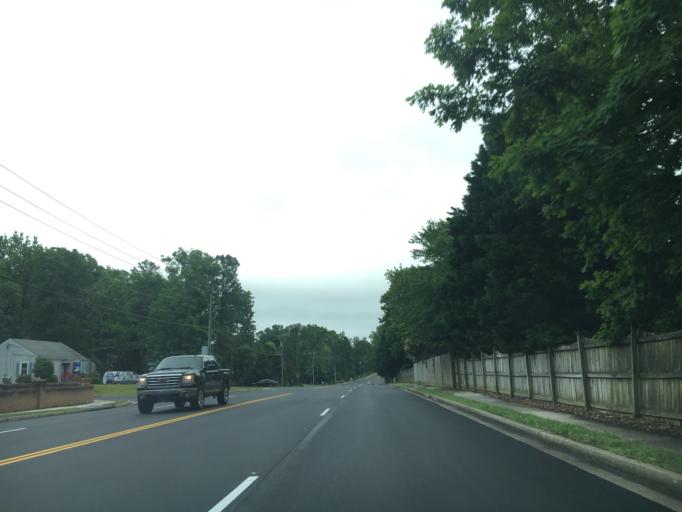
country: US
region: Virginia
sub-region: Henrico County
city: Short Pump
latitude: 37.6343
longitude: -77.6287
